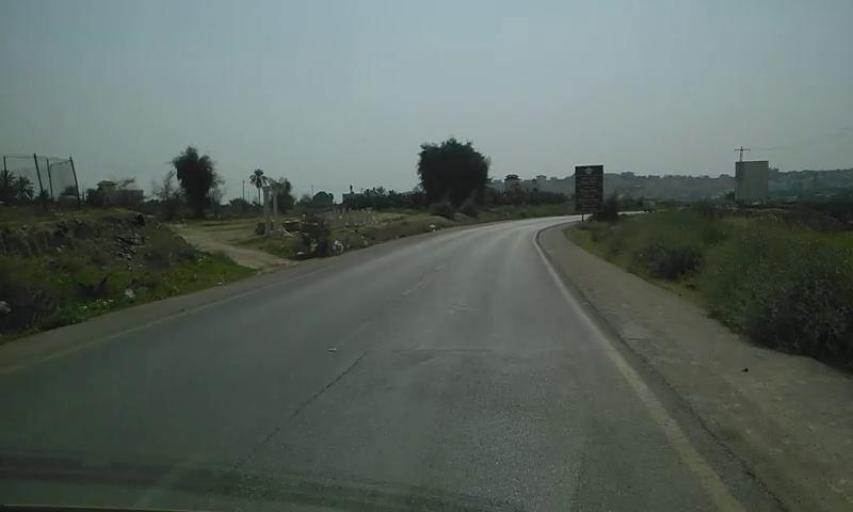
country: PS
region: West Bank
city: An Nuway`imah
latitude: 31.8869
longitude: 35.4347
